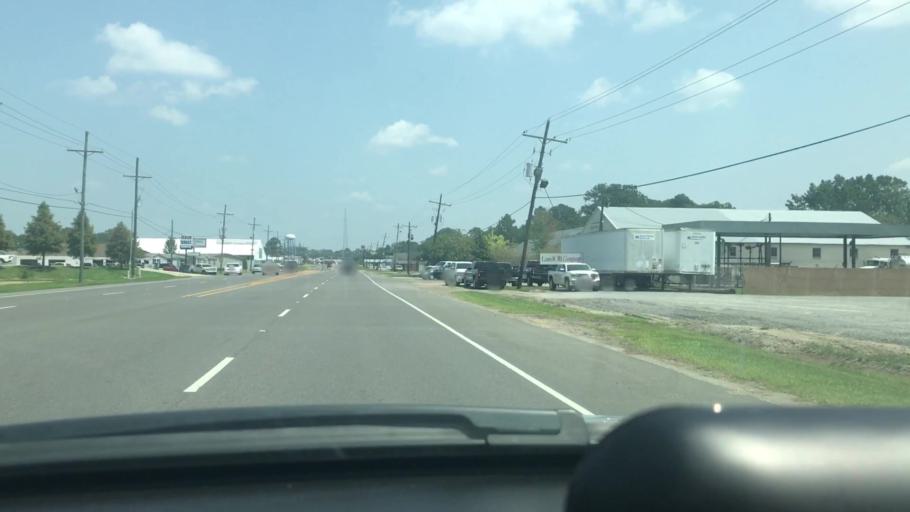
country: US
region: Louisiana
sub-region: Livingston Parish
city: Denham Springs
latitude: 30.4755
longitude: -90.9612
